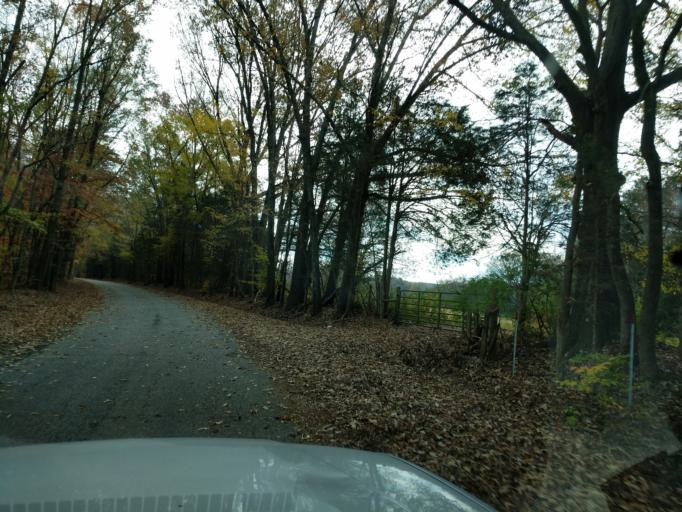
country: US
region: South Carolina
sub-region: Laurens County
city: Watts Mills
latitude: 34.5490
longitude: -81.9448
